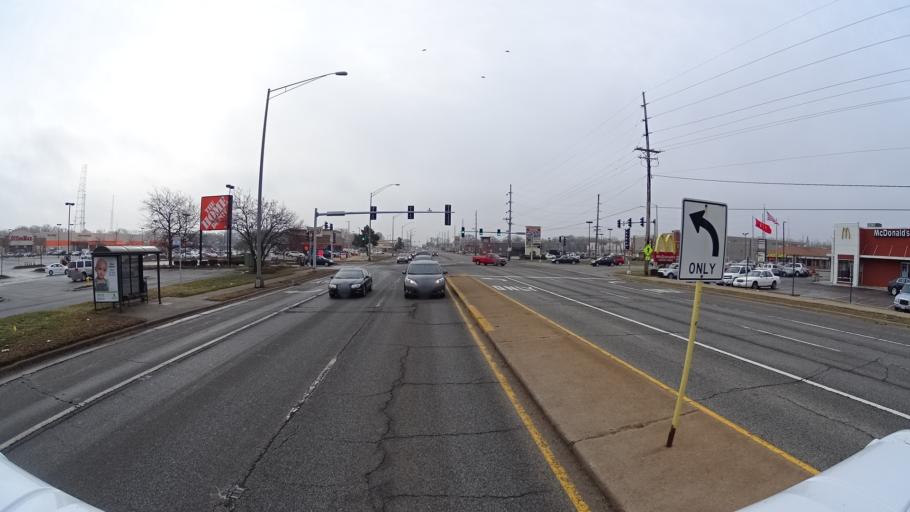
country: US
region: Illinois
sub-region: Cook County
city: East Hazel Crest
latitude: 41.5672
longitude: -87.6362
